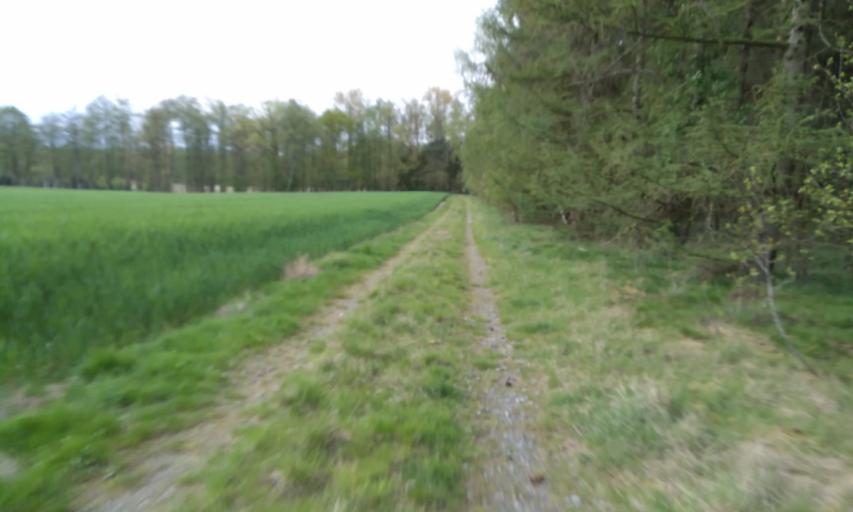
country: DE
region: Lower Saxony
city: Bliedersdorf
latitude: 53.4761
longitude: 9.5322
